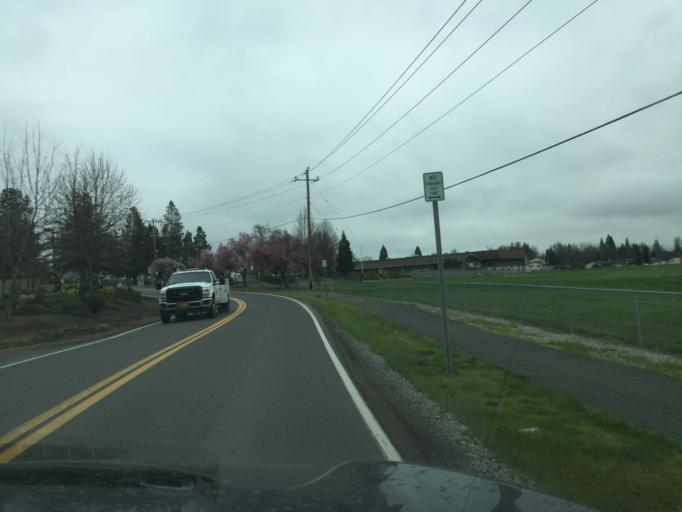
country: US
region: Oregon
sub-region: Jackson County
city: Central Point
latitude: 42.3891
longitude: -122.9253
